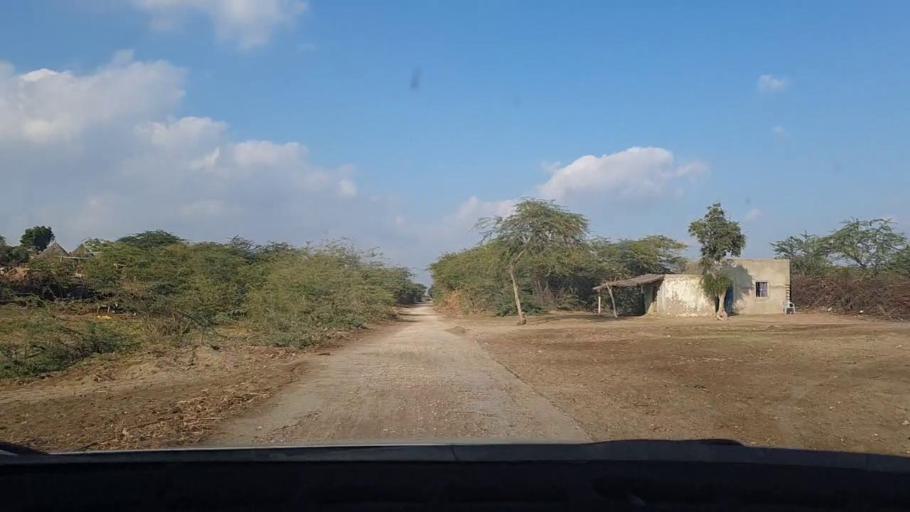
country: PK
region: Sindh
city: Tando Mittha Khan
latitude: 25.8792
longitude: 69.2867
